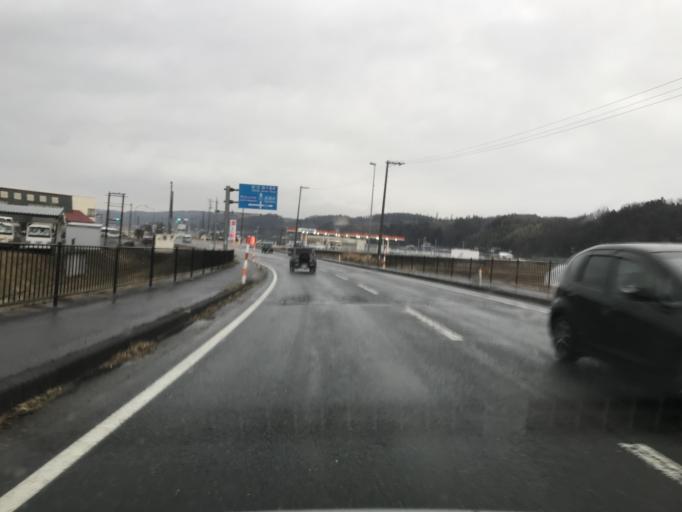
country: JP
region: Miyagi
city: Furukawa
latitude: 38.6558
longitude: 140.8806
